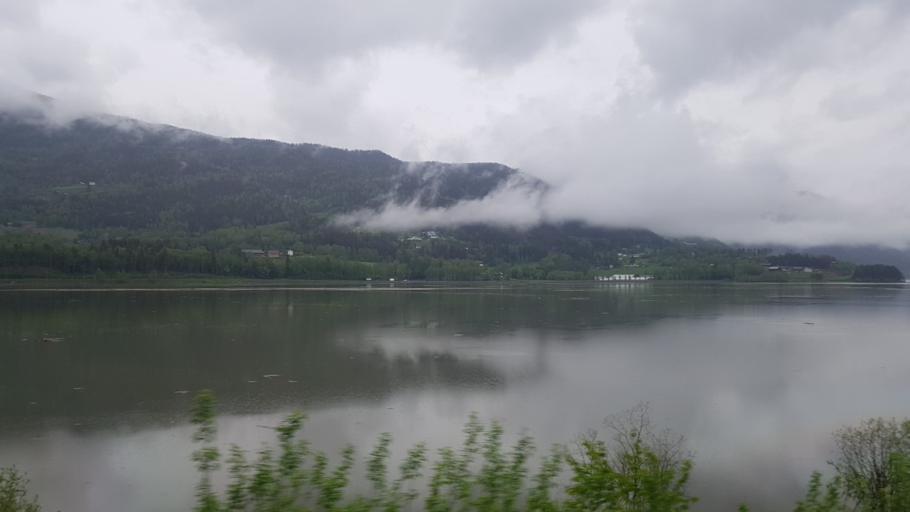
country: NO
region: Oppland
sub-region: Oyer
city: Tretten
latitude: 61.3745
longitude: 10.2685
